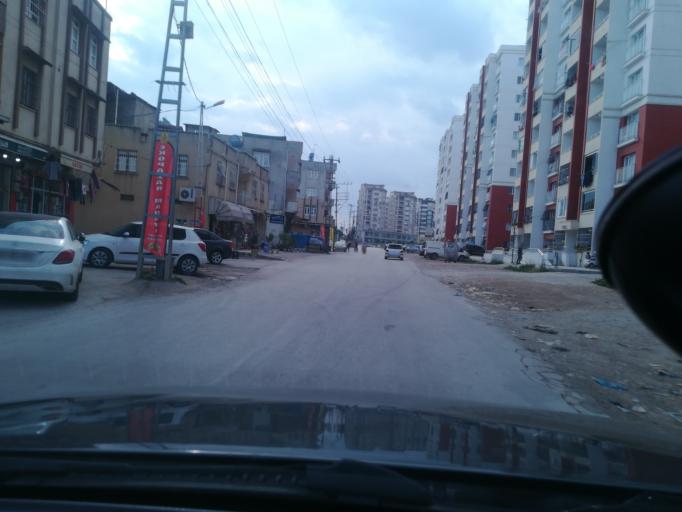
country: TR
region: Adana
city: Seyhan
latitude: 37.0079
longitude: 35.2768
